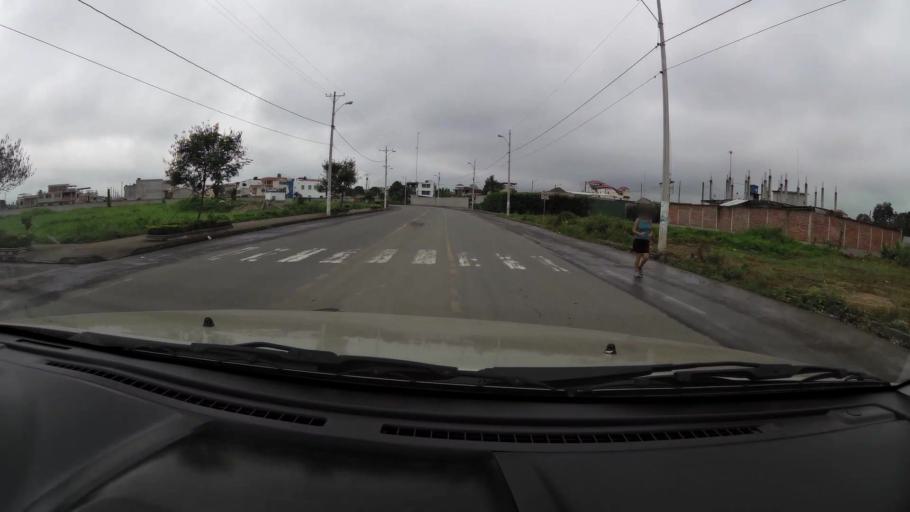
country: EC
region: El Oro
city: Pasaje
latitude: -3.3259
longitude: -79.8187
